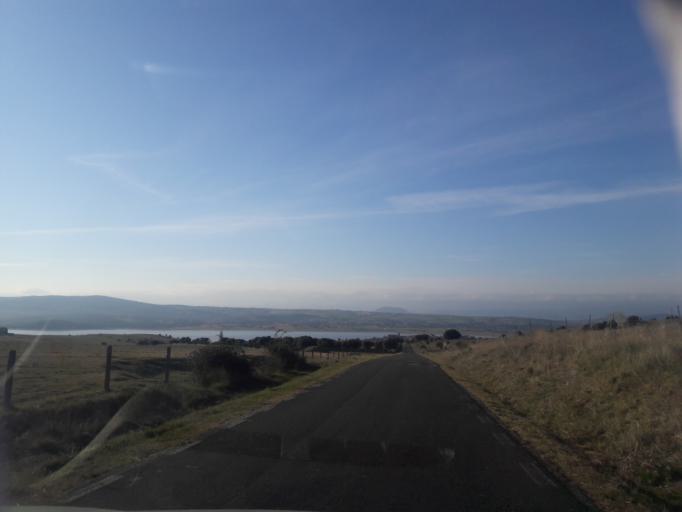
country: ES
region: Castille and Leon
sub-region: Provincia de Salamanca
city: Salvatierra de Tormes
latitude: 40.6036
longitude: -5.6004
